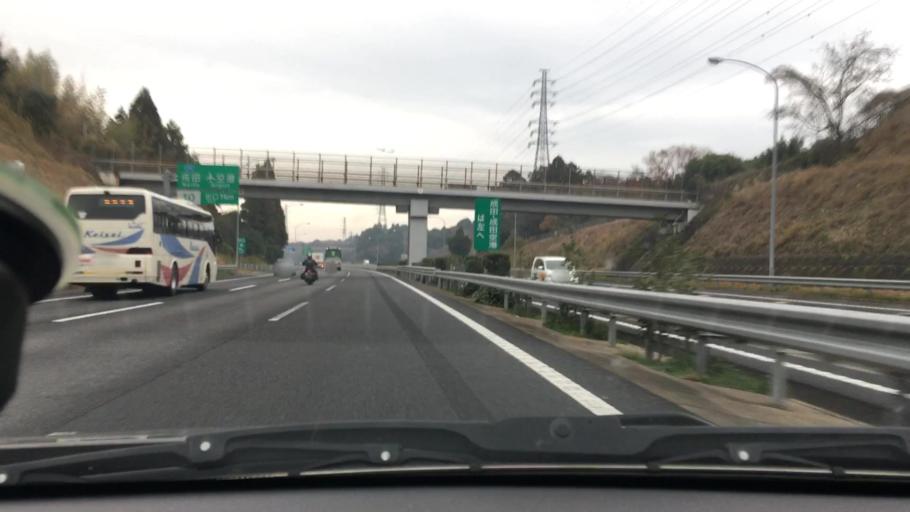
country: JP
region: Chiba
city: Narita
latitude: 35.7712
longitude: 140.3351
